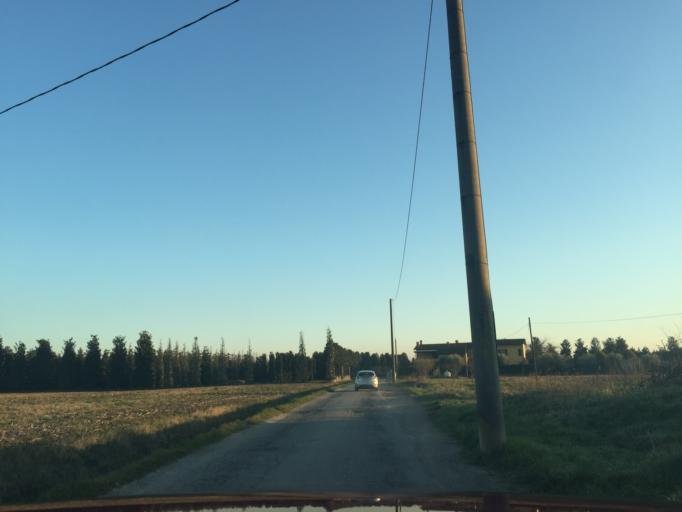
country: IT
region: Tuscany
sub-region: Provincia di Pistoia
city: Ponte Buggianese
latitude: 43.8467
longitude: 10.7554
